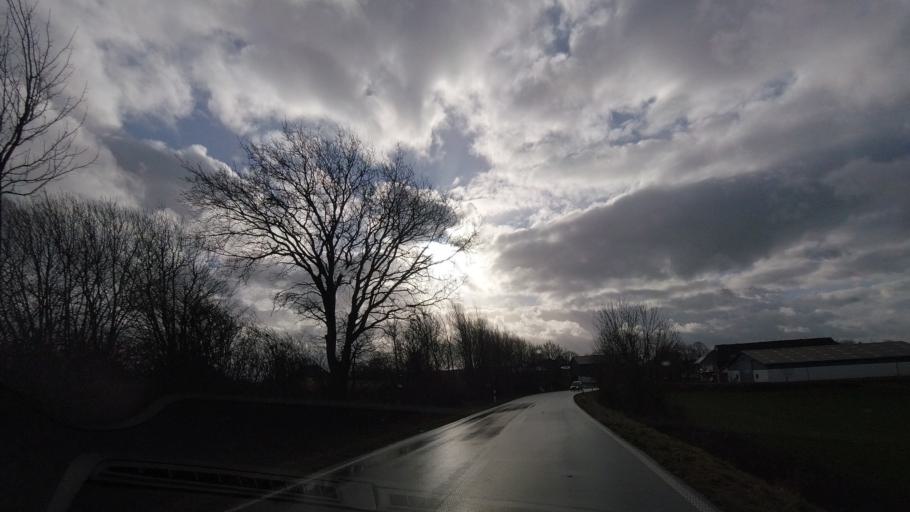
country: DE
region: Schleswig-Holstein
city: Grodersby
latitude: 54.6413
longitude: 9.9206
